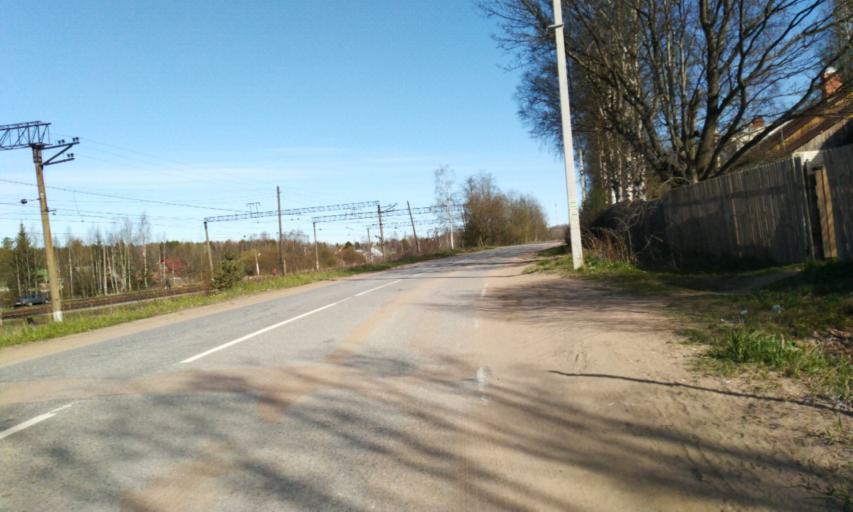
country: RU
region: Leningrad
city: Leskolovo
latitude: 60.3194
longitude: 30.4308
